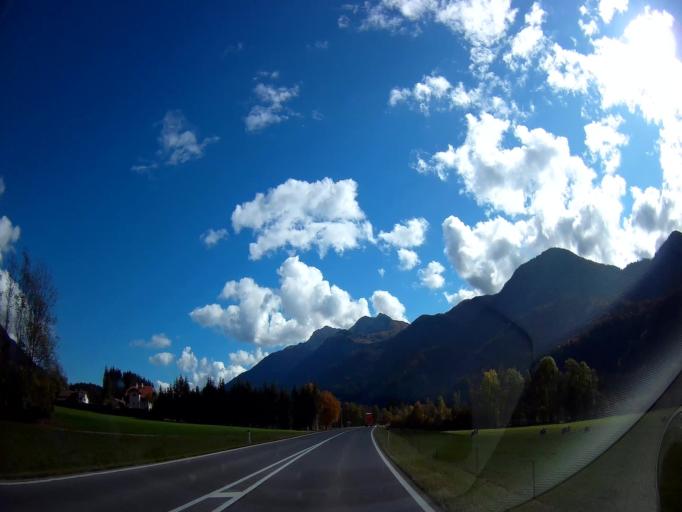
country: AT
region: Carinthia
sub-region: Politischer Bezirk Spittal an der Drau
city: Oberdrauburg
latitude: 46.7488
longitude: 12.9904
